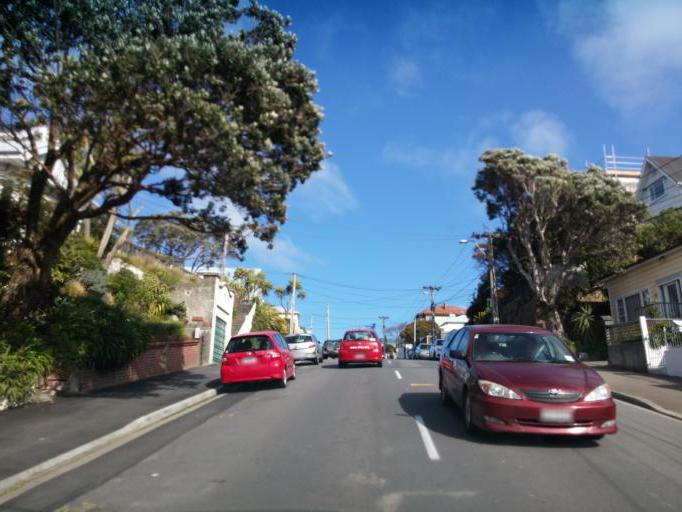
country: NZ
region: Wellington
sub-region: Wellington City
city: Wellington
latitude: -41.3033
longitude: 174.7671
